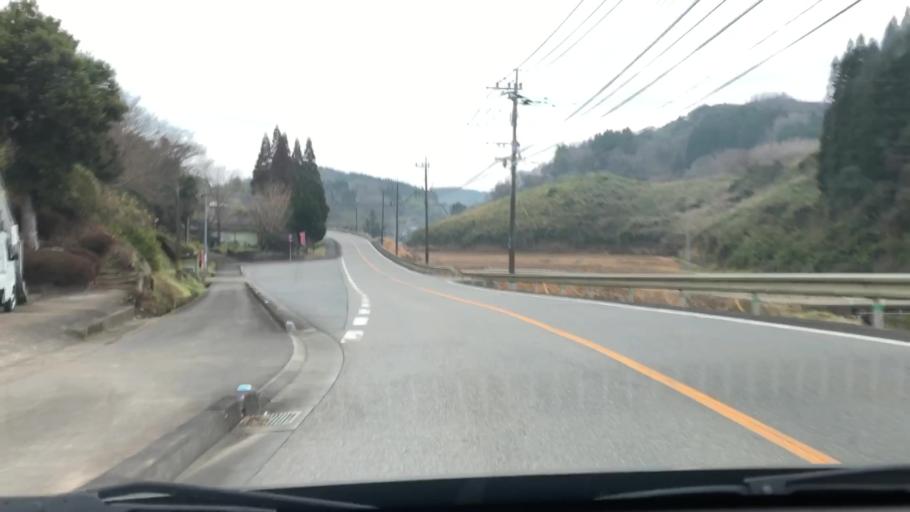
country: JP
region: Oita
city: Usuki
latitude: 33.0088
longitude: 131.6411
